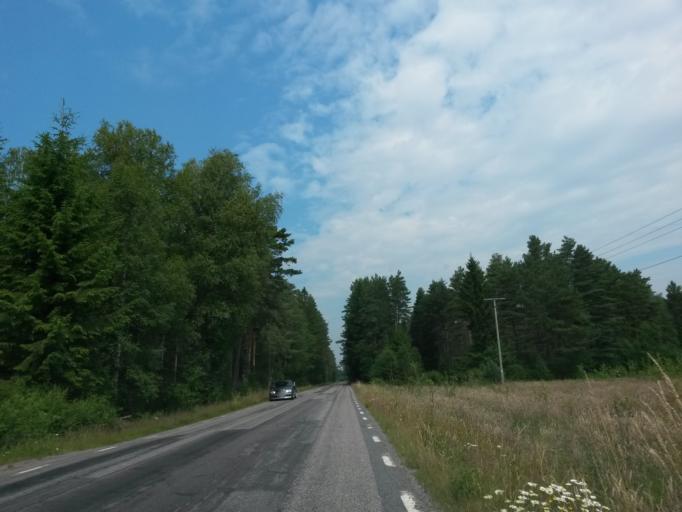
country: SE
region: Vaestra Goetaland
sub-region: Essunga Kommun
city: Nossebro
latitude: 58.1665
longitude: 12.7444
